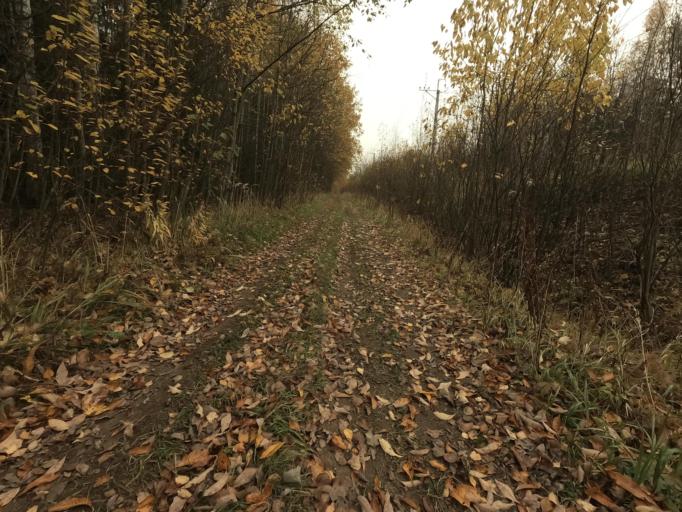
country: RU
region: Leningrad
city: Pavlovo
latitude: 59.7715
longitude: 30.9094
